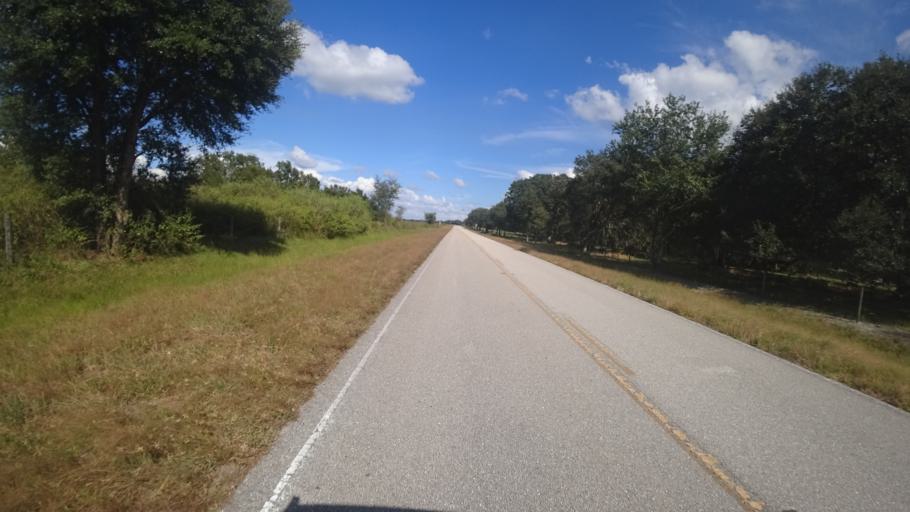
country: US
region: Florida
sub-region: DeSoto County
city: Arcadia
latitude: 27.2738
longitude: -82.0606
